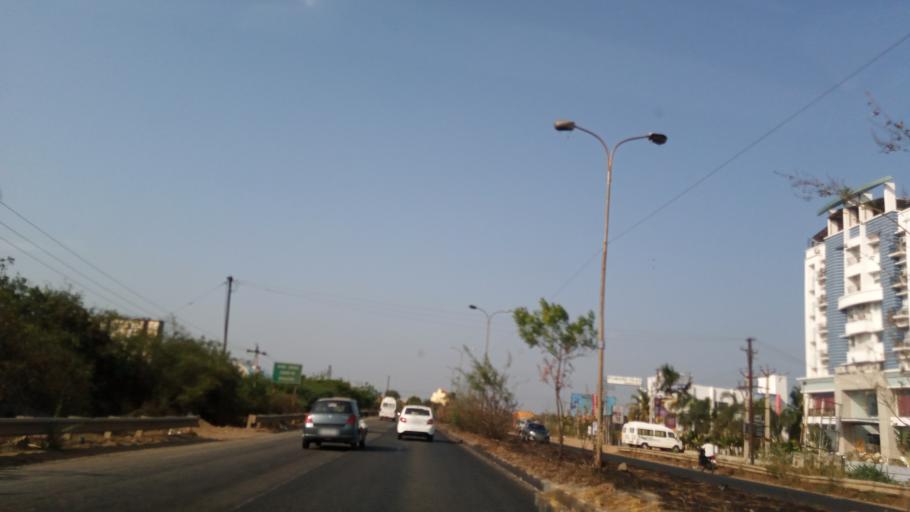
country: IN
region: Tamil Nadu
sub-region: Kancheepuram
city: Sriperumbudur
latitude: 13.0101
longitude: 79.9979
